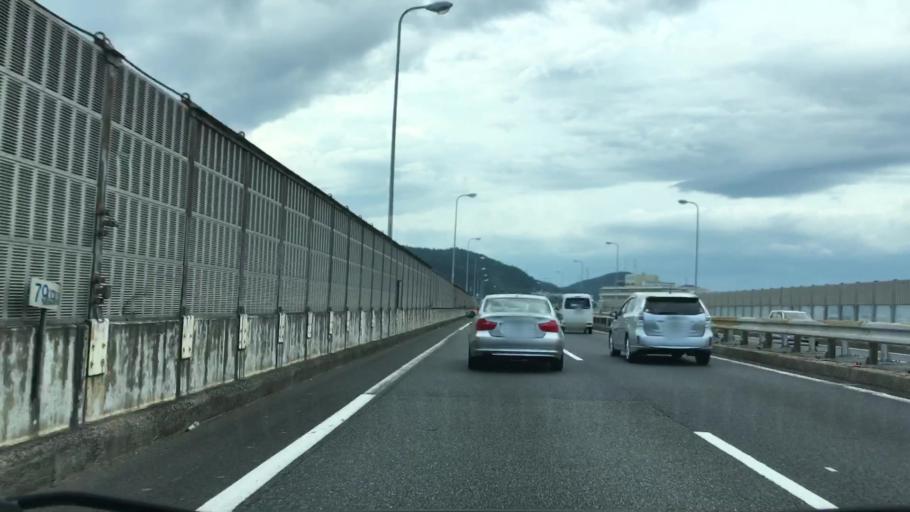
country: JP
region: Hyogo
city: Kakogawacho-honmachi
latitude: 34.7869
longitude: 134.7765
